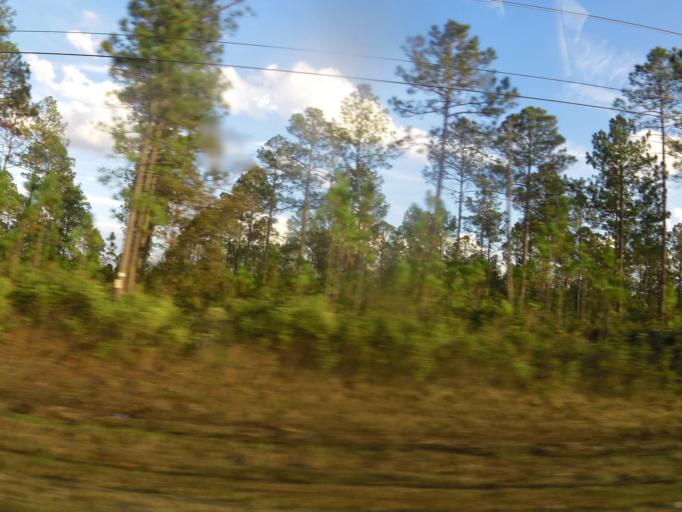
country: US
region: Florida
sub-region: Duval County
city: Baldwin
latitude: 30.1709
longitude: -81.9953
